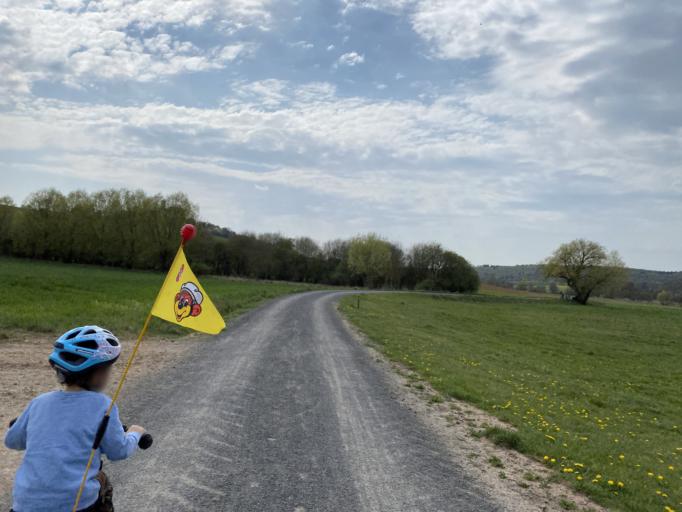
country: DE
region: Hesse
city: Budingen
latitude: 50.2470
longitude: 9.0669
